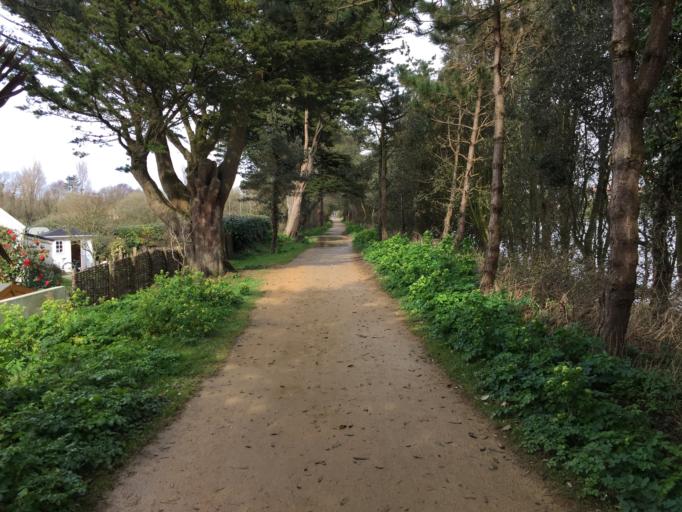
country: JE
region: St Helier
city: Saint Helier
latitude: 49.1846
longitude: -2.2227
